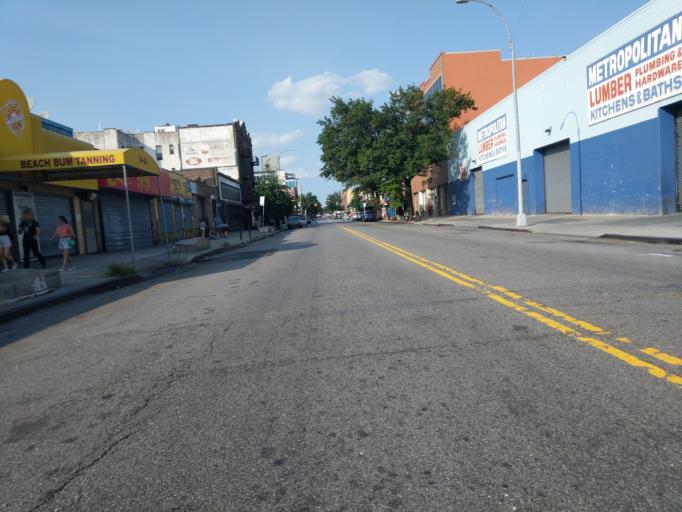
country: US
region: New York
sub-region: Queens County
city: Long Island City
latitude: 40.7554
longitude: -73.9219
